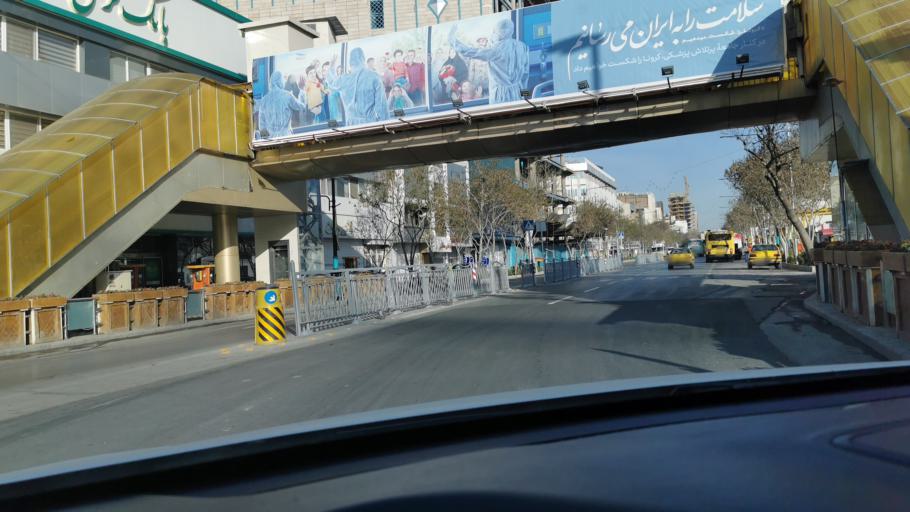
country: IR
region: Razavi Khorasan
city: Mashhad
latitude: 36.2843
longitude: 59.6119
